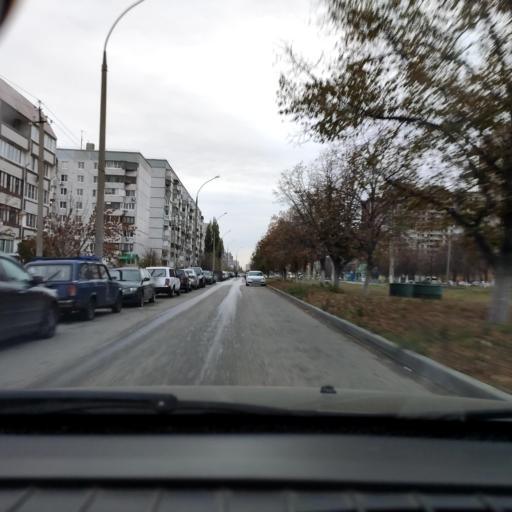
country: RU
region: Samara
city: Tol'yatti
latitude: 53.5431
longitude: 49.3246
